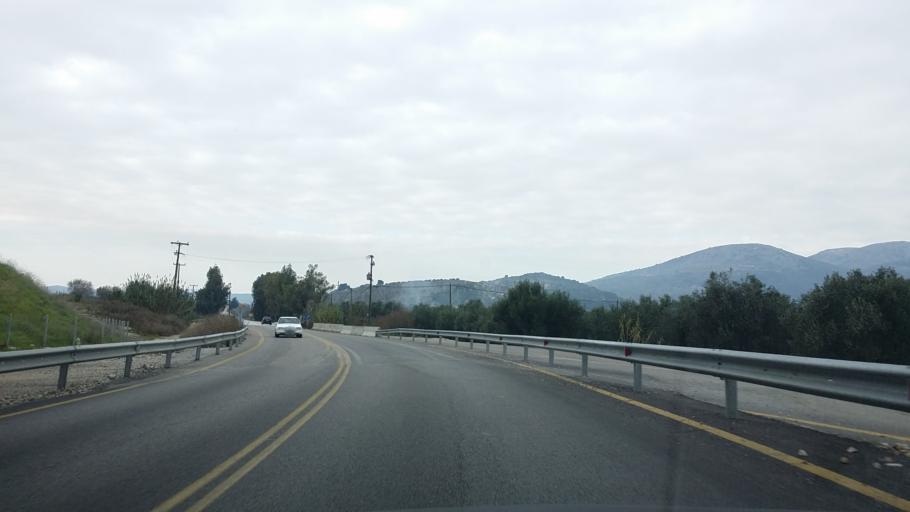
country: GR
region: West Greece
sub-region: Nomos Aitolias kai Akarnanias
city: Mesolongi
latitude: 38.3934
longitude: 21.4287
